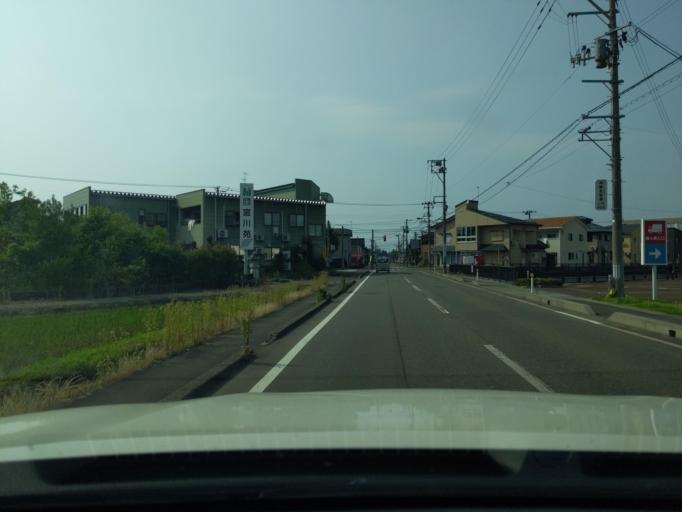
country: JP
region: Niigata
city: Nagaoka
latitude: 37.4294
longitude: 138.8607
